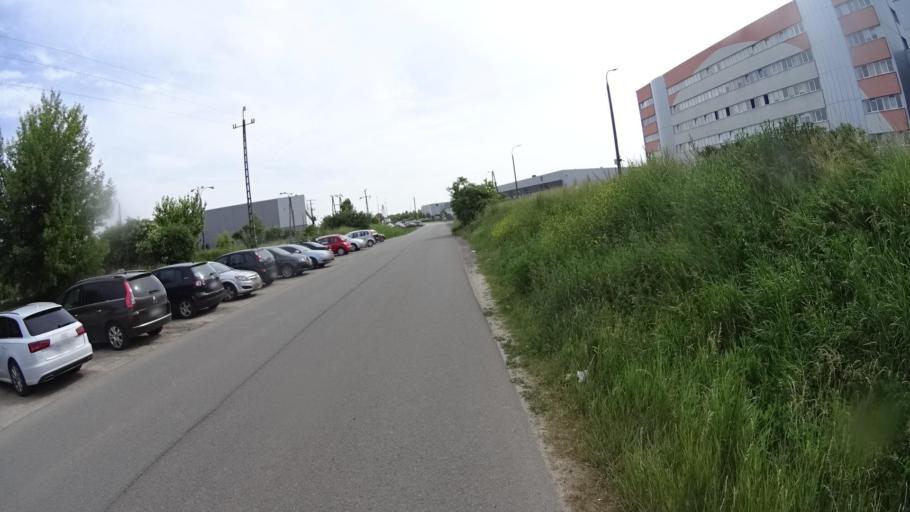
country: PL
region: Masovian Voivodeship
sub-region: Warszawa
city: Wlochy
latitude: 52.1897
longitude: 20.9352
